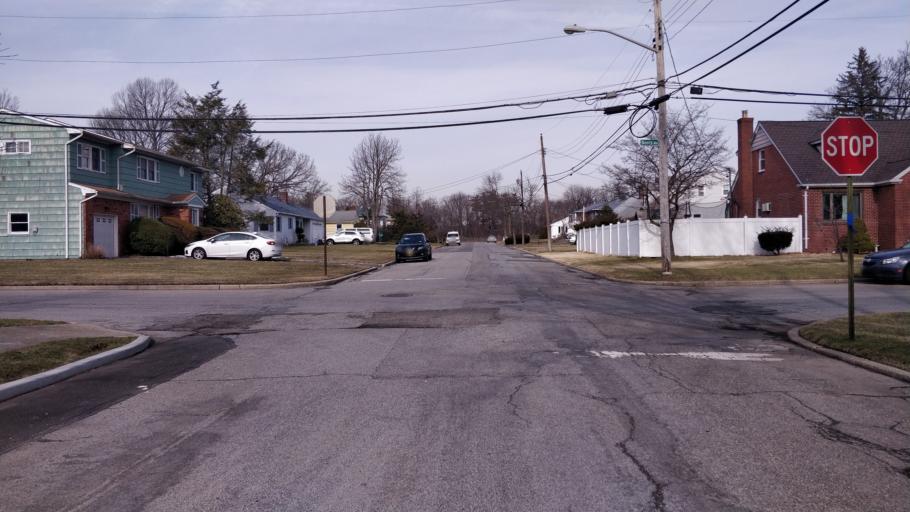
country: US
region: New York
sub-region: Nassau County
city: Hicksville
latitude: 40.7826
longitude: -73.5276
